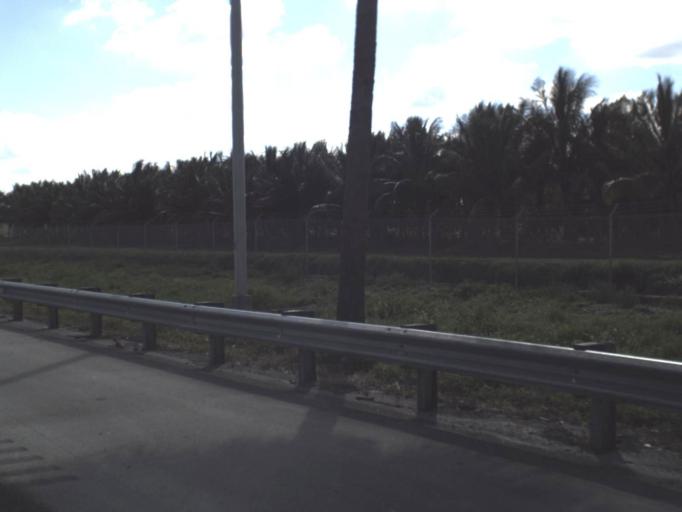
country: US
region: Florida
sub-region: Palm Beach County
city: Villages of Oriole
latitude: 26.5017
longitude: -80.1727
